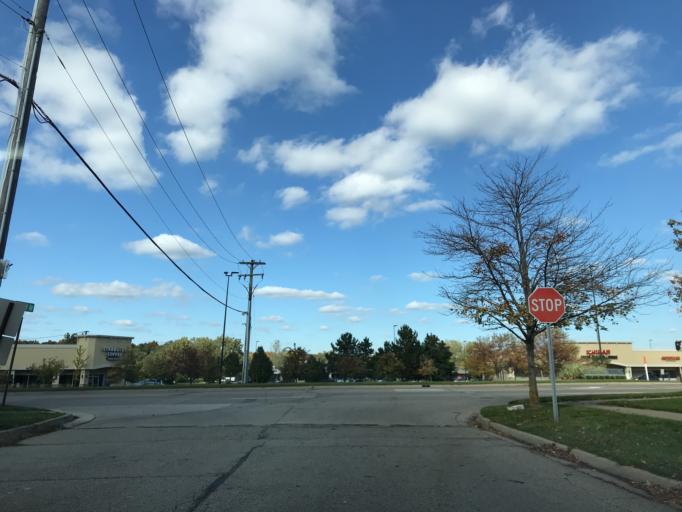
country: US
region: Michigan
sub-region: Washtenaw County
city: Ypsilanti
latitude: 42.2514
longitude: -83.6691
